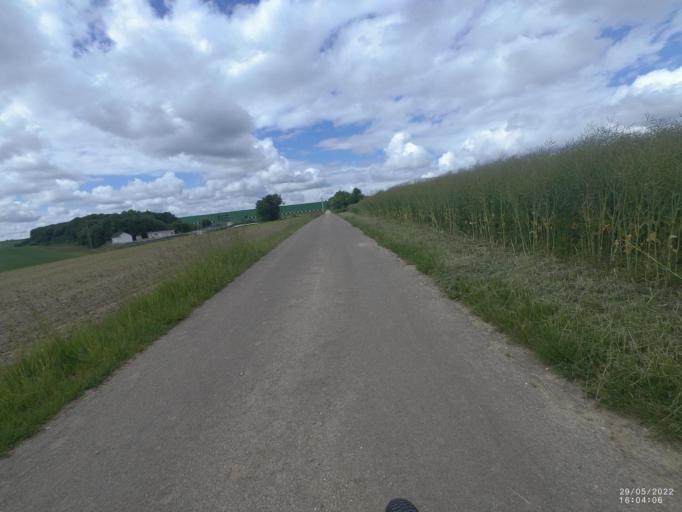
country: DE
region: Baden-Wuerttemberg
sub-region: Tuebingen Region
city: Setzingen
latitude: 48.5851
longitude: 10.1243
